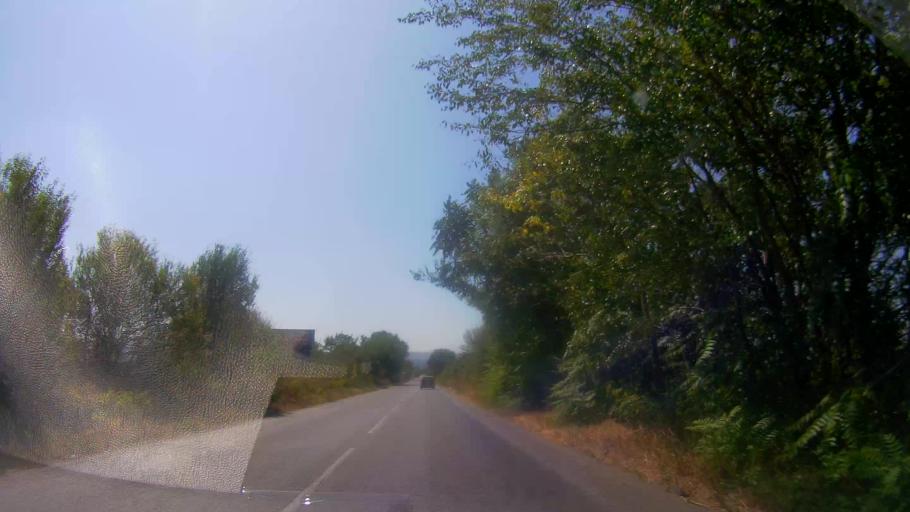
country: BG
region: Veliko Turnovo
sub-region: Obshtina Gorna Oryakhovitsa
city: Purvomaytsi
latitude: 43.2284
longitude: 25.6393
